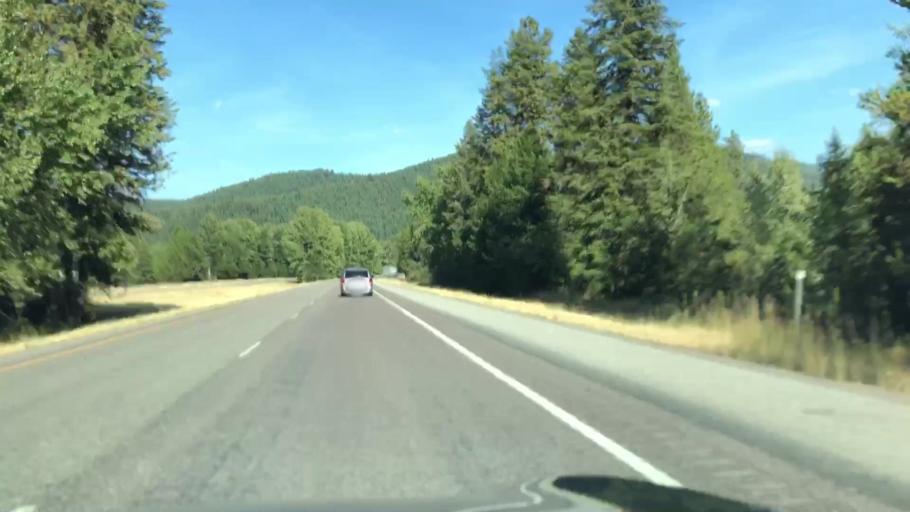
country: US
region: Montana
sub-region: Sanders County
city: Thompson Falls
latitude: 47.3778
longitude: -115.3636
